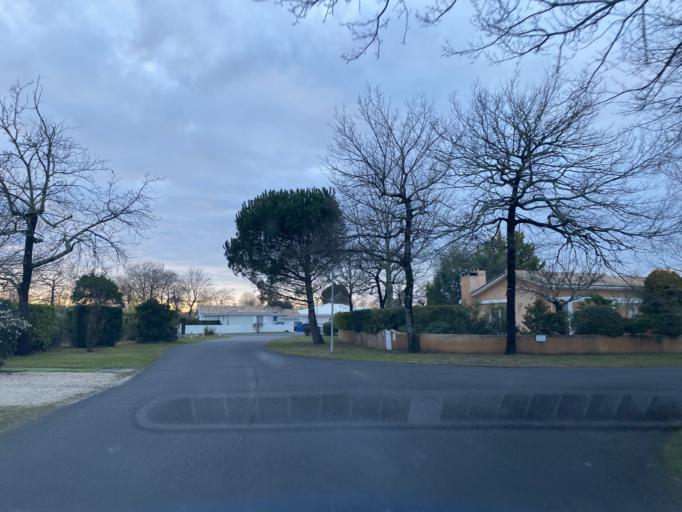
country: FR
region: Aquitaine
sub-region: Departement de la Gironde
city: Andernos-les-Bains
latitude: 44.7521
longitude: -1.0832
